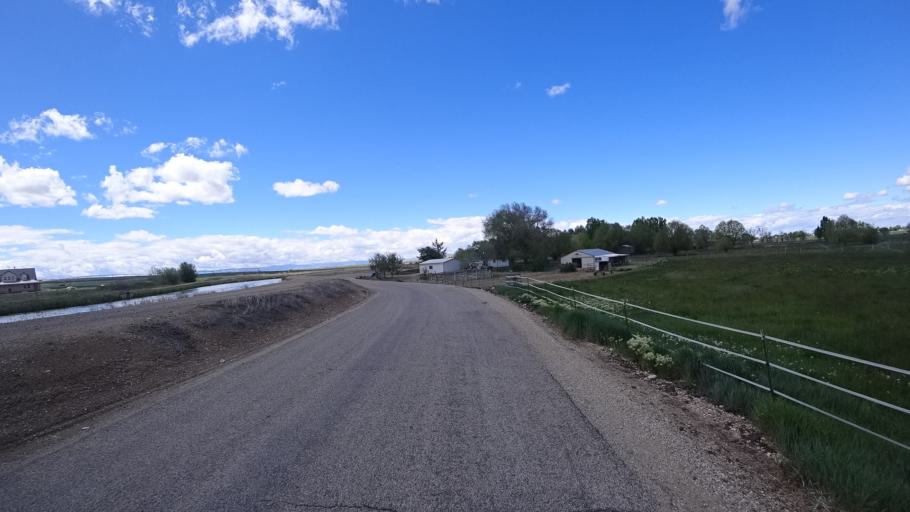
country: US
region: Idaho
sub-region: Ada County
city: Kuna
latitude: 43.4595
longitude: -116.3757
